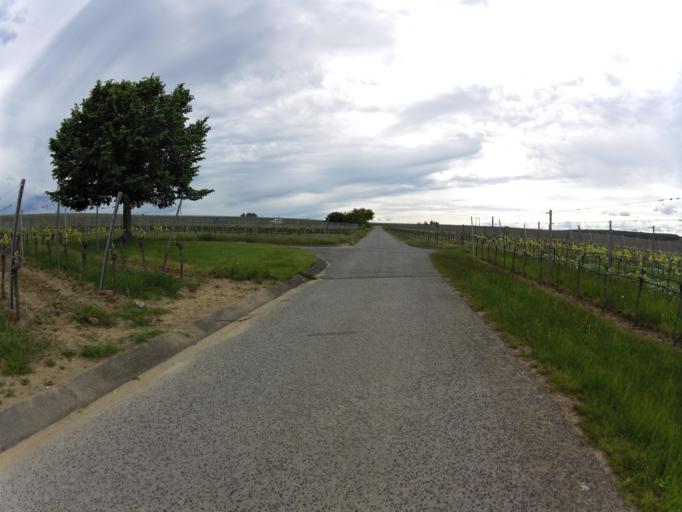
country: DE
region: Bavaria
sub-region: Regierungsbezirk Unterfranken
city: Nordheim
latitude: 49.8521
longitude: 10.1968
